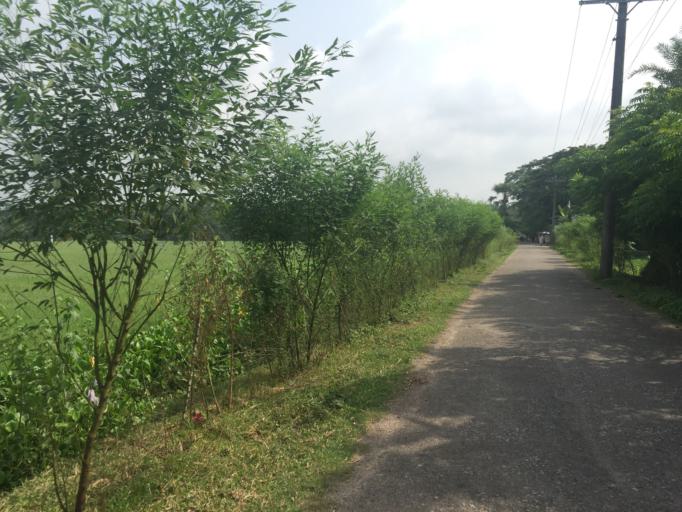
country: BD
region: Barisal
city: Mathba
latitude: 22.2474
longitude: 89.9134
